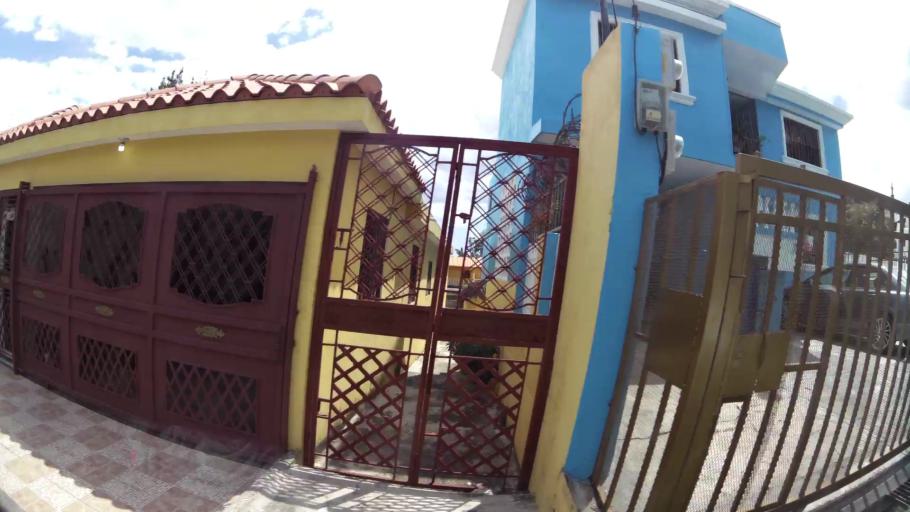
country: DO
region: Nacional
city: Ensanche Luperon
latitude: 18.5241
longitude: -69.9105
